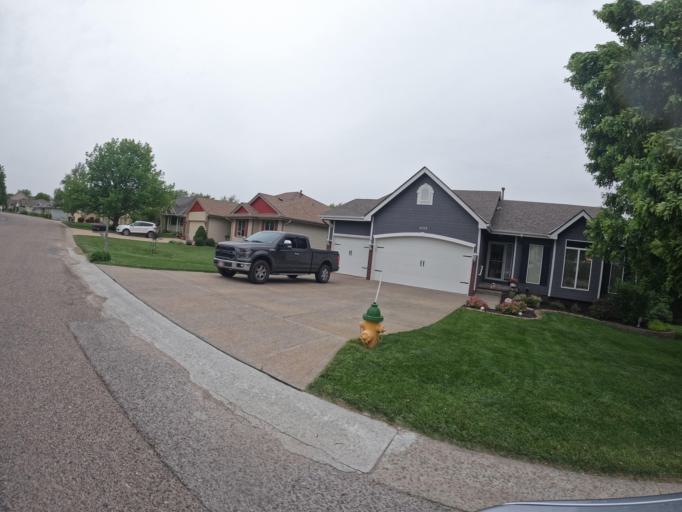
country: US
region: Nebraska
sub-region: Sarpy County
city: Offutt Air Force Base
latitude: 41.0485
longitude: -95.9740
